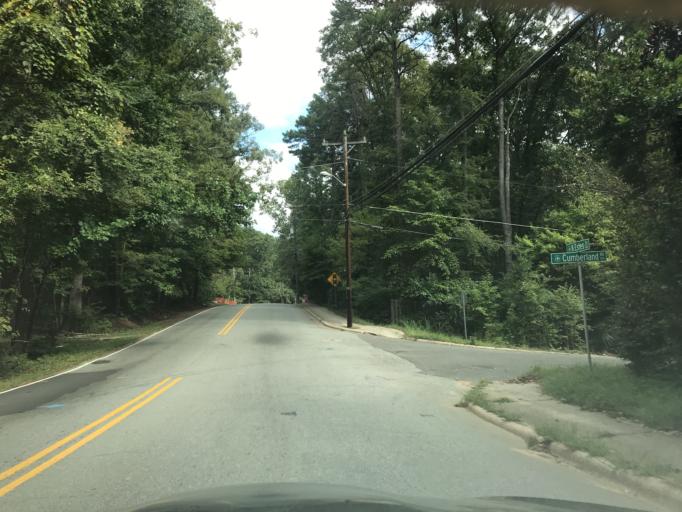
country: US
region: North Carolina
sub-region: Orange County
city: Chapel Hill
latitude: 35.9351
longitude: -79.0460
